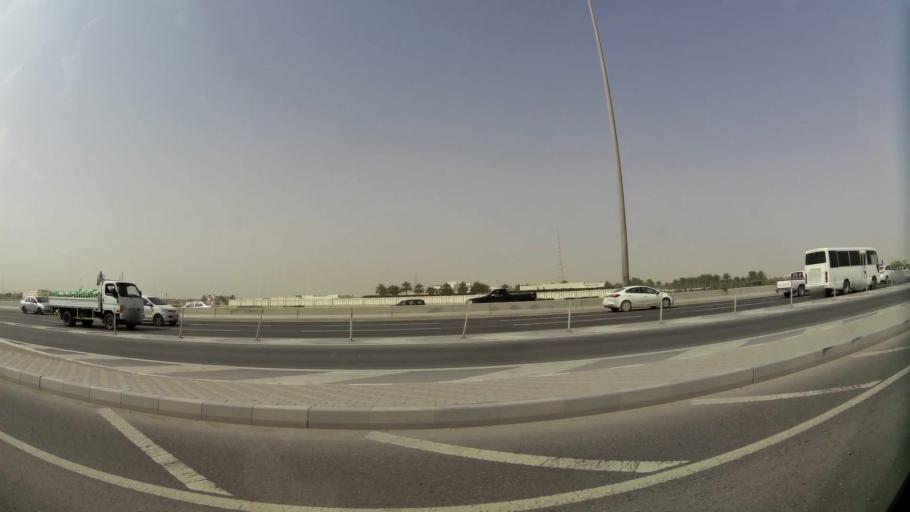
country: QA
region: Baladiyat ad Dawhah
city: Doha
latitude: 25.2854
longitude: 51.4827
